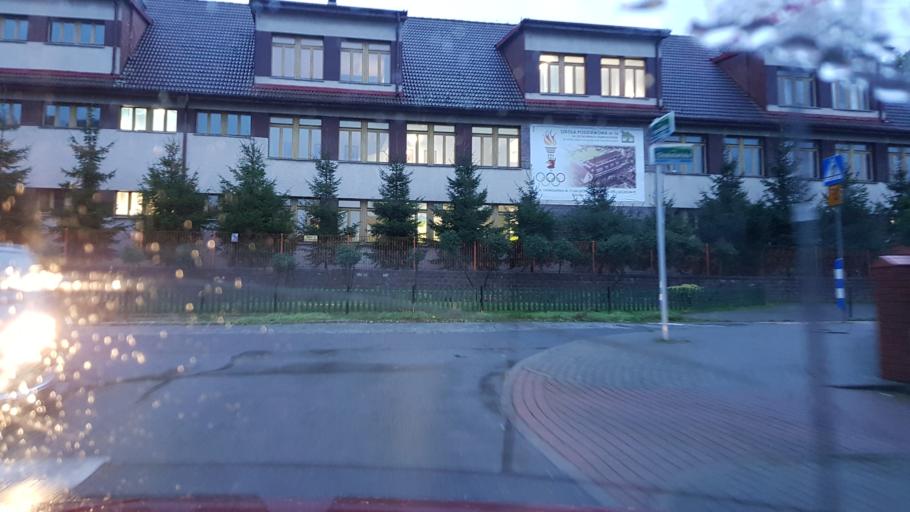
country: PL
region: West Pomeranian Voivodeship
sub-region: Powiat policki
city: Przeclaw
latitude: 53.4117
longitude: 14.4994
